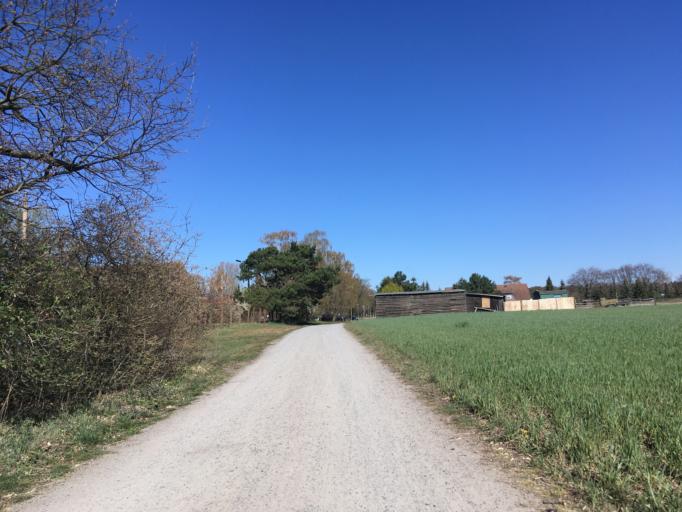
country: DE
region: Berlin
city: Buch
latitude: 52.6763
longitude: 13.4790
